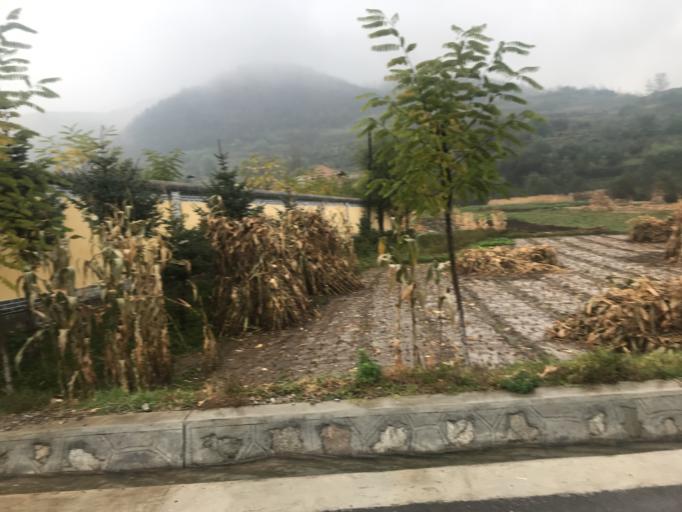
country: CN
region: Gansu Sheng
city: Maji
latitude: 35.3921
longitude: 103.0642
